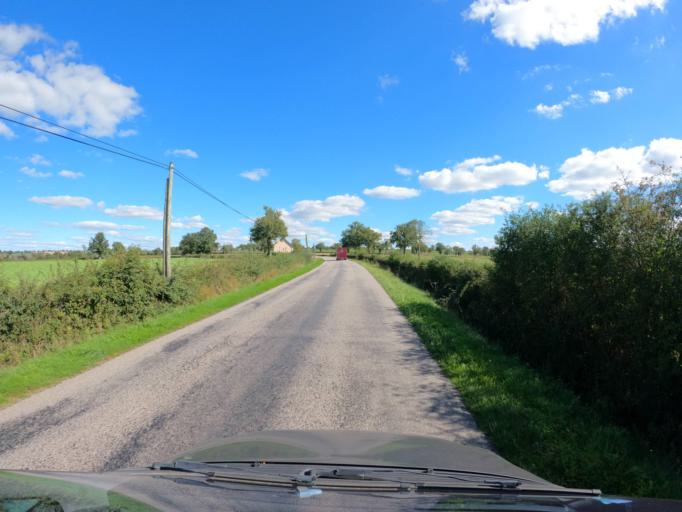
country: FR
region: Auvergne
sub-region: Departement de l'Allier
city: Buxieres-les-Mines
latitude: 46.4039
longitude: 2.9160
